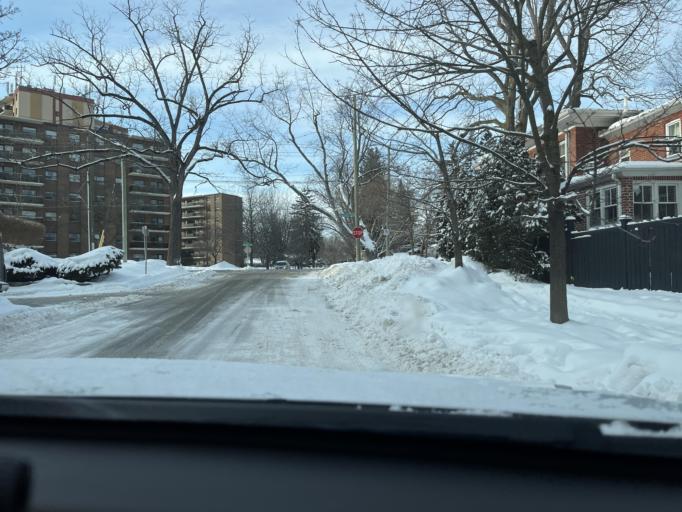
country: CA
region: Ontario
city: Oakville
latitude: 43.4495
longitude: -79.6635
